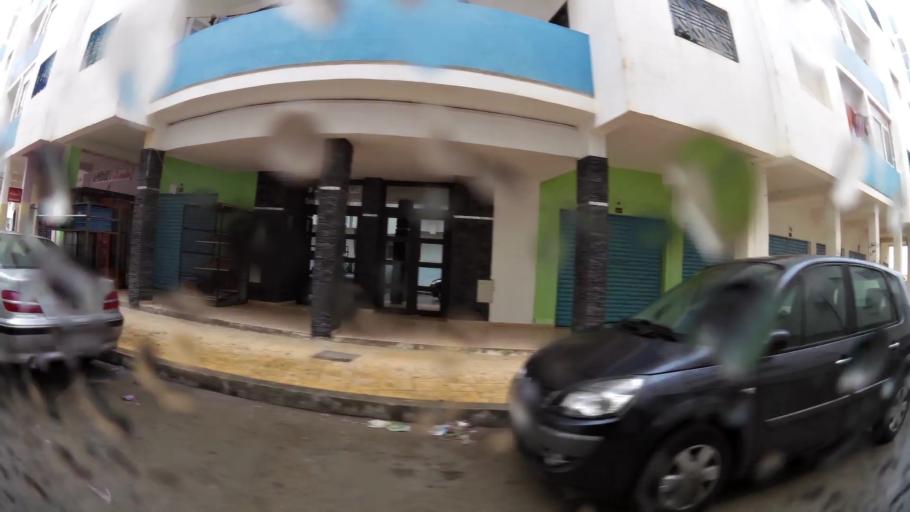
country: MA
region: Tanger-Tetouan
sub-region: Tetouan
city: Martil
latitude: 35.6190
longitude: -5.2827
